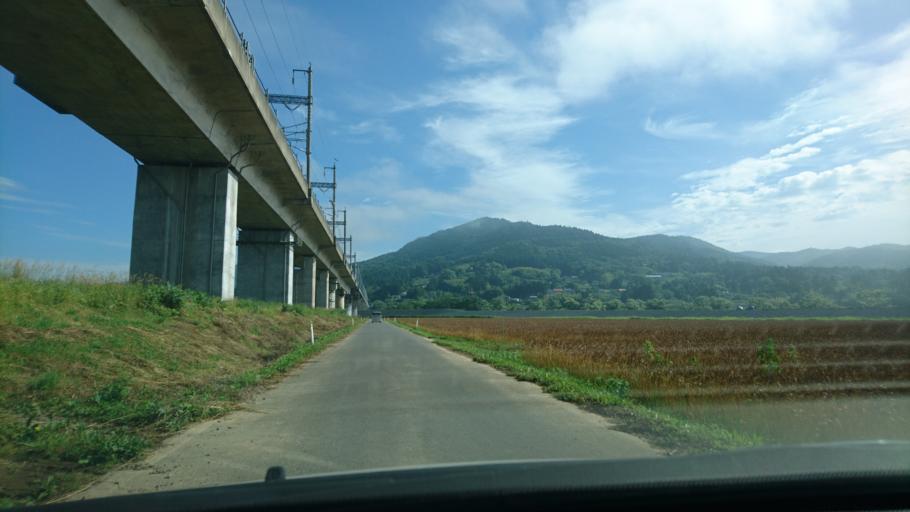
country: JP
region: Iwate
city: Ichinoseki
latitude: 38.9693
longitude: 141.1545
